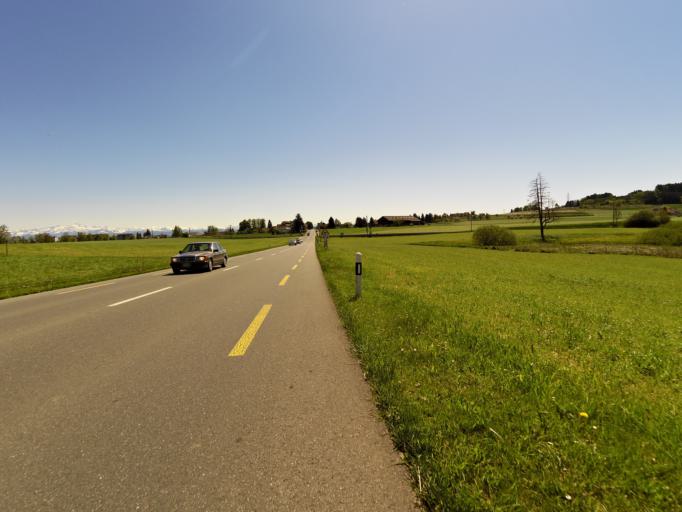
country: CH
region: Thurgau
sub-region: Weinfelden District
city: Berg
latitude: 47.5878
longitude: 9.1703
